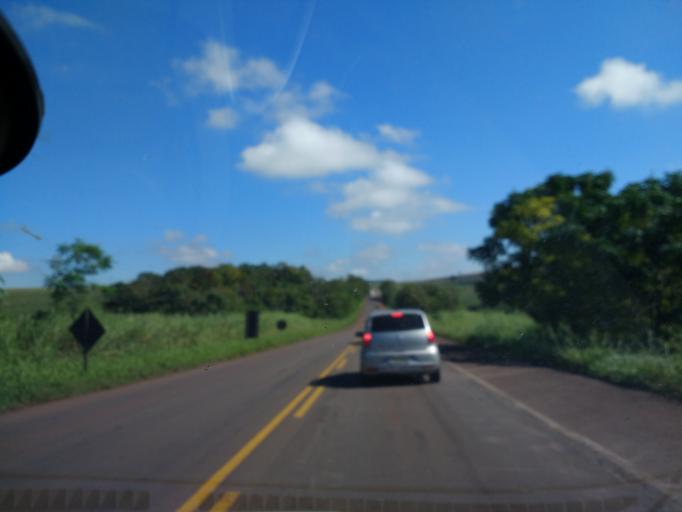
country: BR
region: Parana
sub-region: Terra Boa
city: Terra Boa
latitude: -23.5973
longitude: -52.3746
